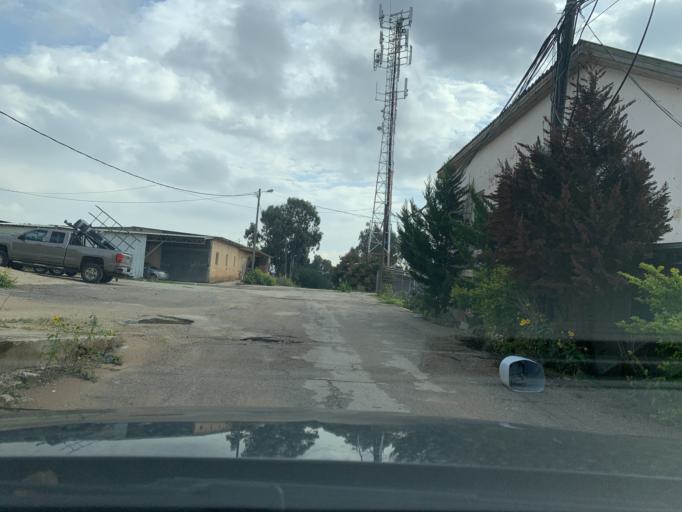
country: PS
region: West Bank
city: Qalqilyah
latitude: 32.1955
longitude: 34.9504
